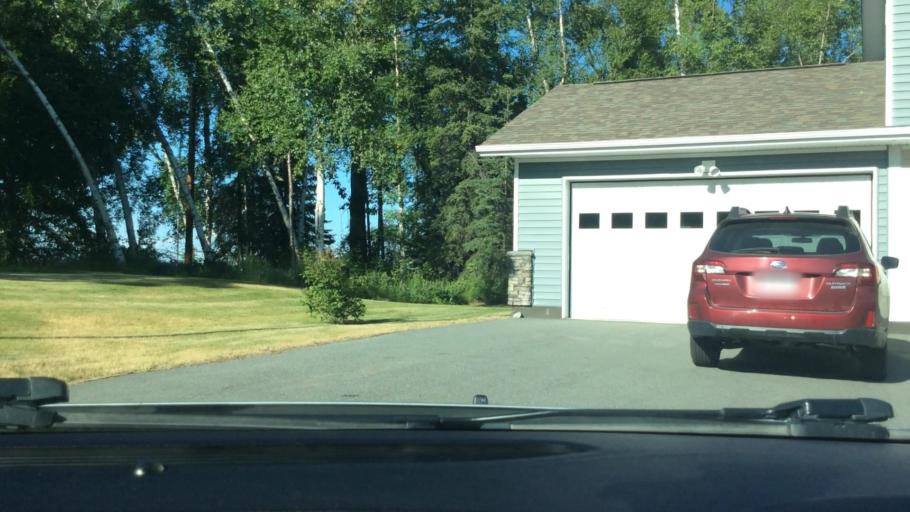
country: US
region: Alaska
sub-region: Anchorage Municipality
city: Elmendorf Air Force Base
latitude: 61.2528
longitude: -149.7003
